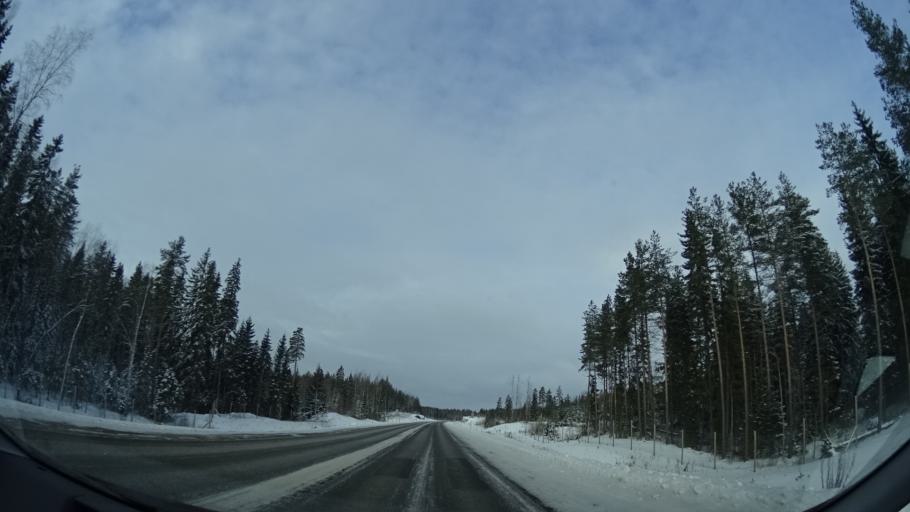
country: FI
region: Uusimaa
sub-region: Helsinki
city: Karkkila
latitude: 60.5918
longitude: 24.1056
